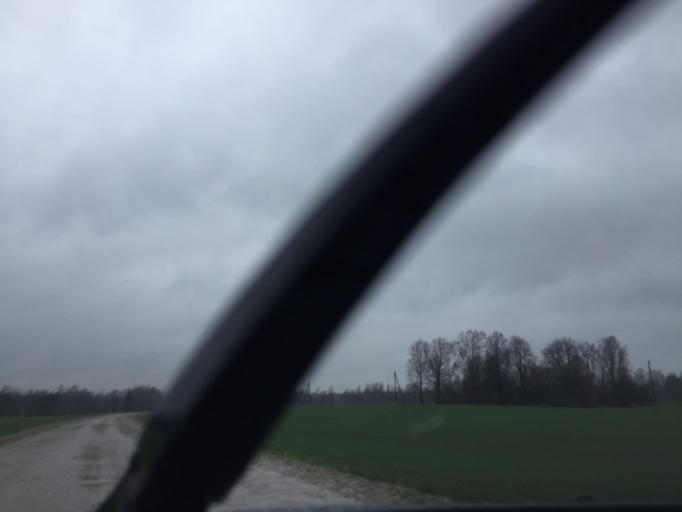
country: LV
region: Salacgrivas
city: Salacgriva
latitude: 57.7670
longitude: 24.5339
